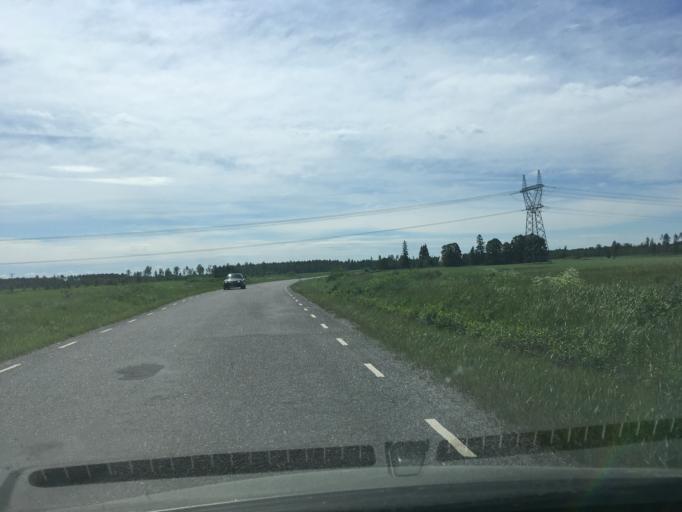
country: EE
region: Paernumaa
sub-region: Audru vald
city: Audru
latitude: 58.4350
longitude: 24.3995
